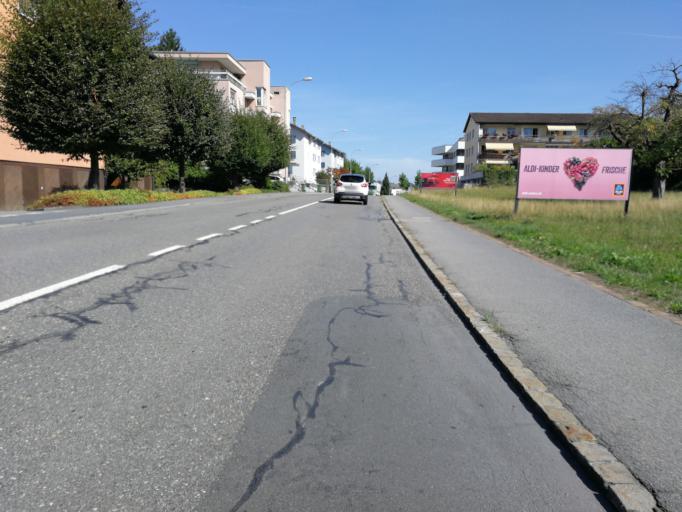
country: CH
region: Schwyz
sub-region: Bezirk Kuessnacht
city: Kussnacht
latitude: 47.0720
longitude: 8.4380
